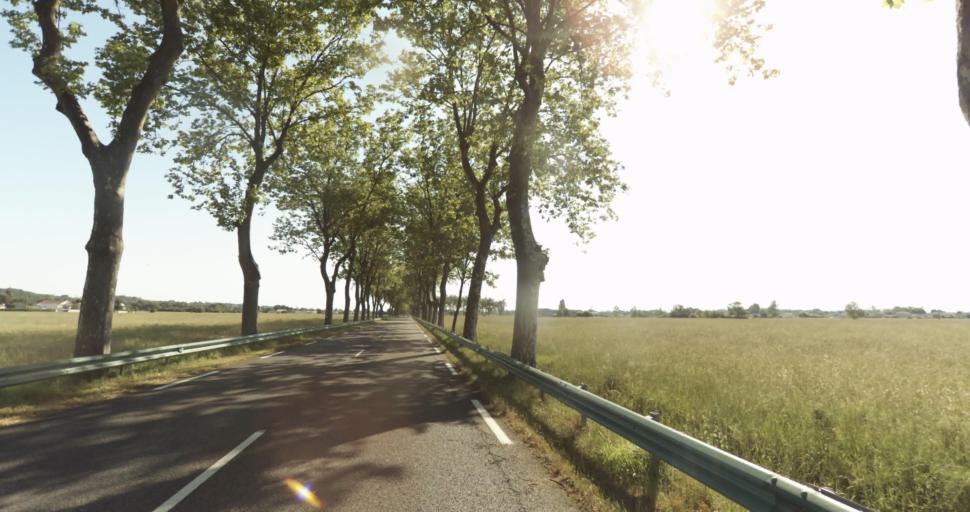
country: FR
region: Midi-Pyrenees
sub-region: Departement de la Haute-Garonne
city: La Salvetat-Saint-Gilles
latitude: 43.5534
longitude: 1.2672
